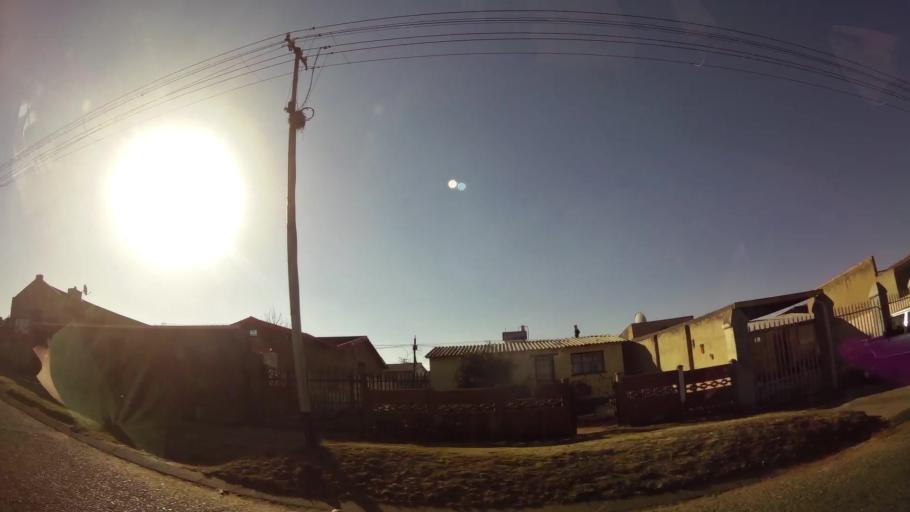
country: ZA
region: Gauteng
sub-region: City of Johannesburg Metropolitan Municipality
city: Johannesburg
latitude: -26.2121
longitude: 27.9728
